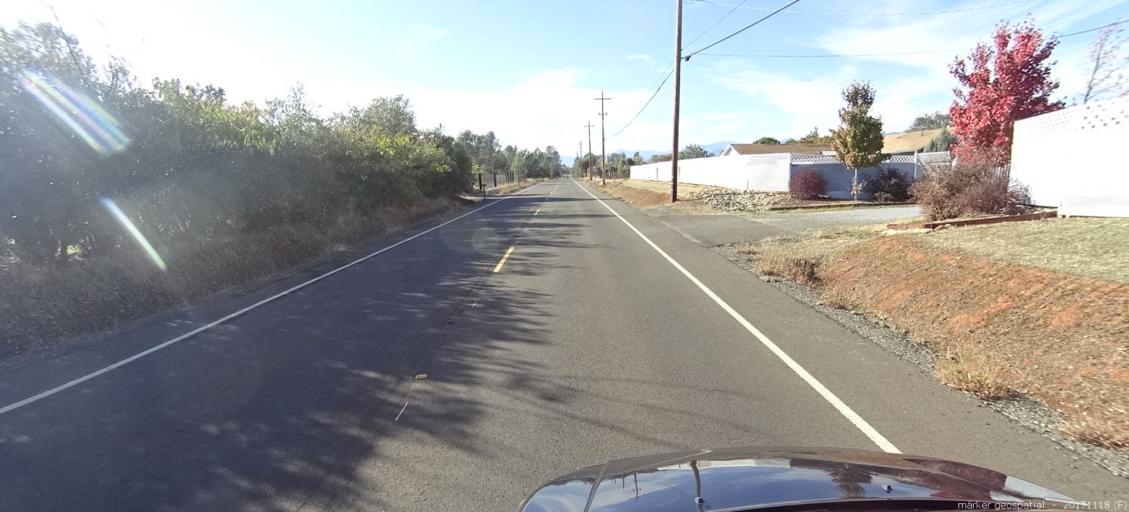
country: US
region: California
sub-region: Shasta County
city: Redding
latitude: 40.4779
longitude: -122.4038
